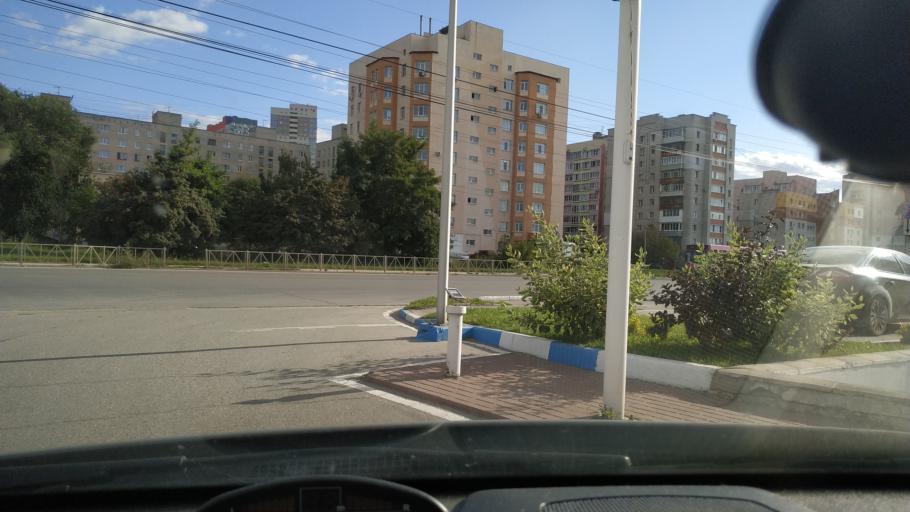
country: RU
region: Rjazan
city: Ryazan'
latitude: 54.6196
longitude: 39.6986
